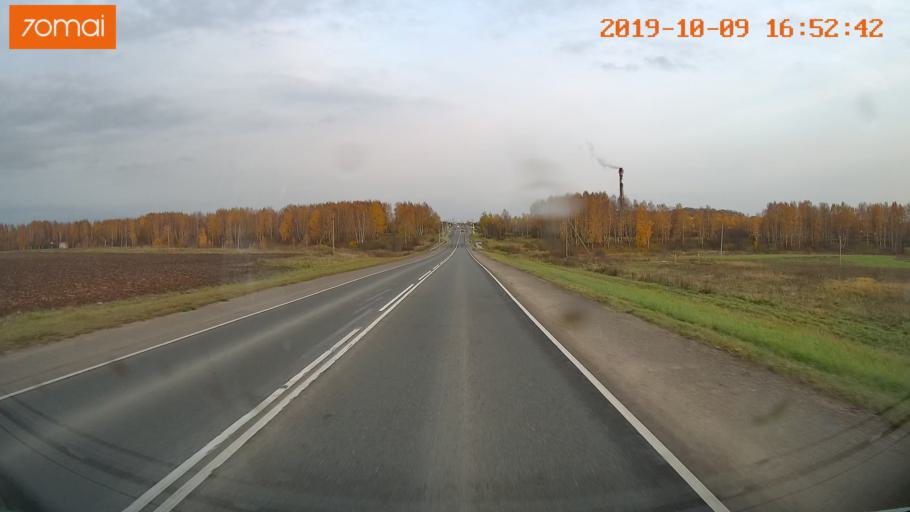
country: RU
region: Ivanovo
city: Privolzhsk
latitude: 57.3794
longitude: 41.2538
